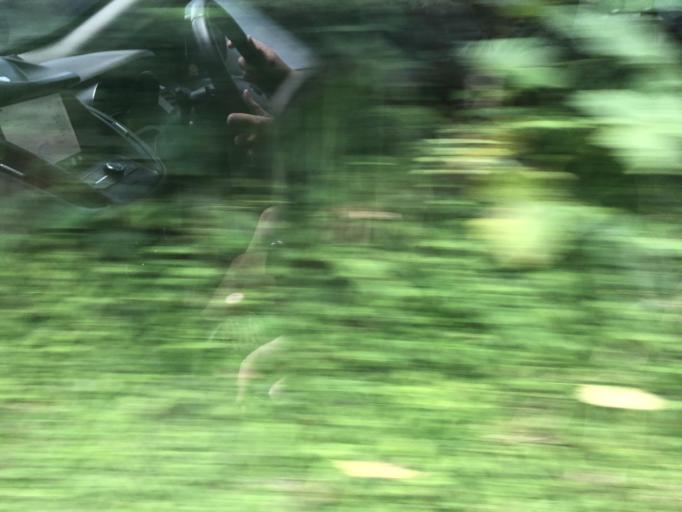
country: TW
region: Taiwan
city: Daxi
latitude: 24.8646
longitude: 121.4221
